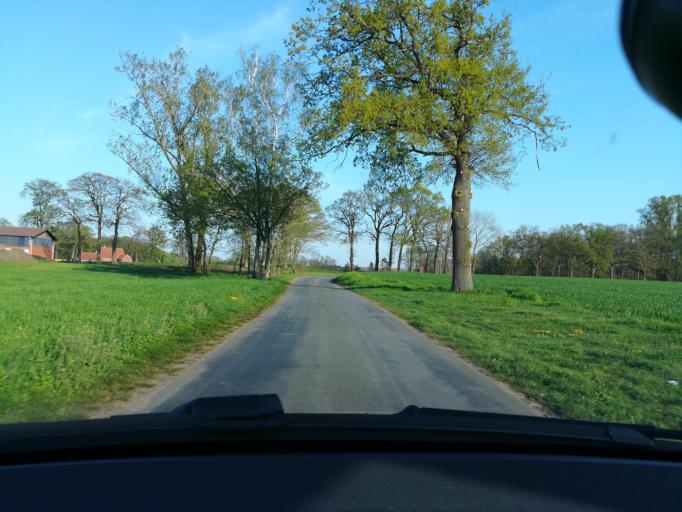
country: DE
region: North Rhine-Westphalia
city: Versmold
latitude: 52.0185
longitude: 8.1023
